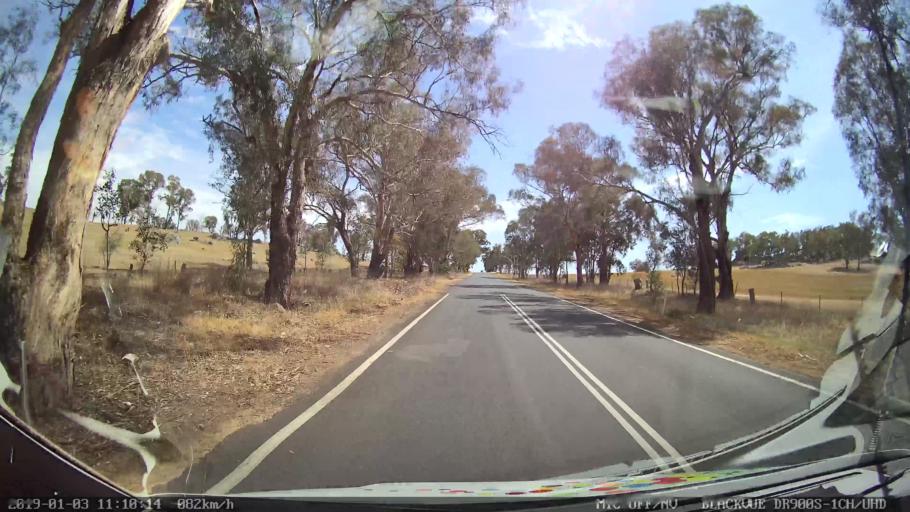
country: AU
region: New South Wales
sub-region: Young
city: Young
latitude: -34.2290
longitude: 148.2579
